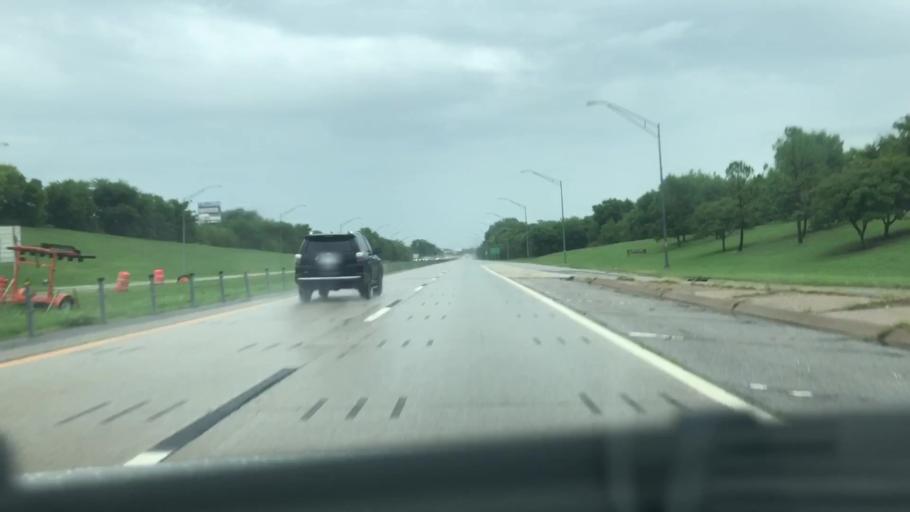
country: US
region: Oklahoma
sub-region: Tulsa County
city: Tulsa
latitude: 36.1782
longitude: -95.9711
